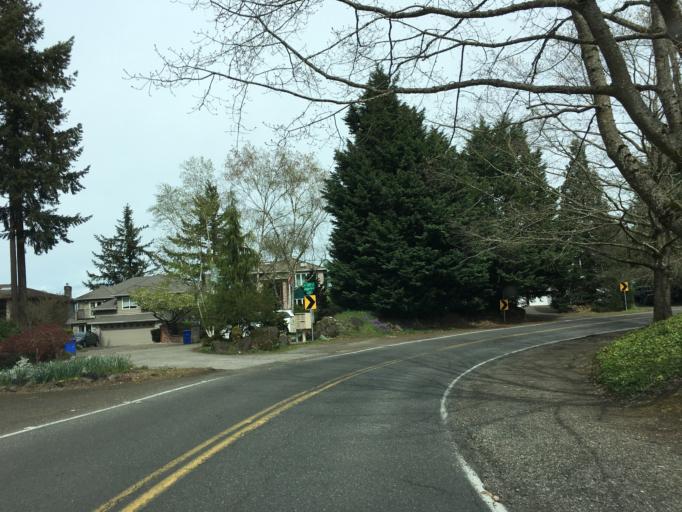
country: US
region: Oregon
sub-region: Multnomah County
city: Lents
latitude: 45.5517
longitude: -122.5690
